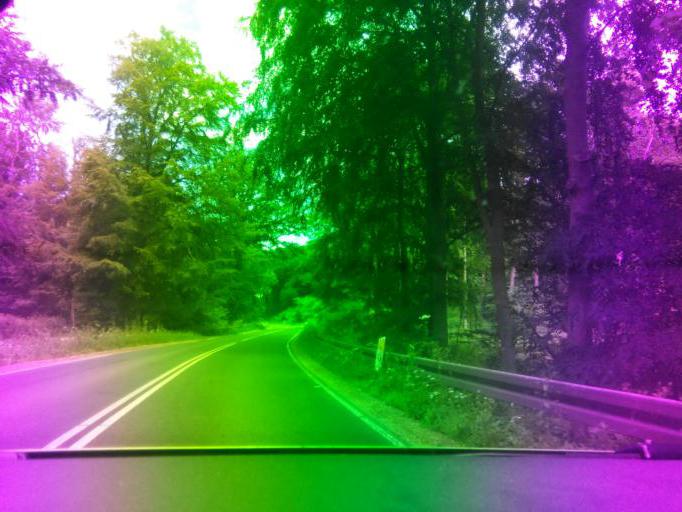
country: DK
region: Zealand
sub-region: Kalundborg Kommune
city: Hong
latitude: 55.5766
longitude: 11.3164
